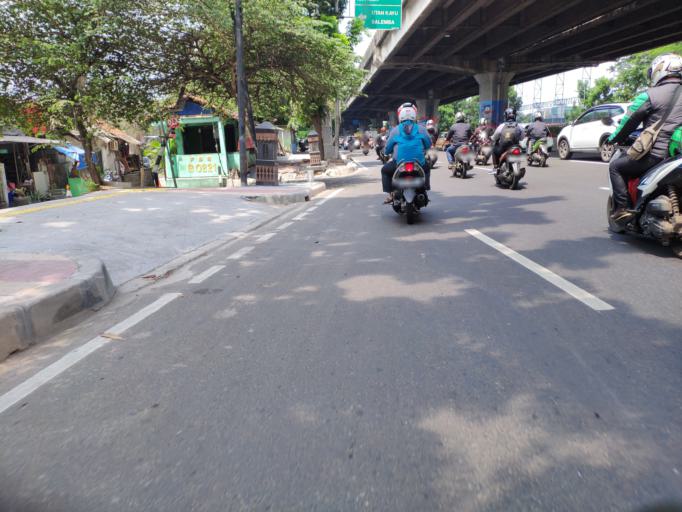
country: ID
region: Jakarta Raya
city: Jakarta
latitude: -6.1998
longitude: 106.8734
